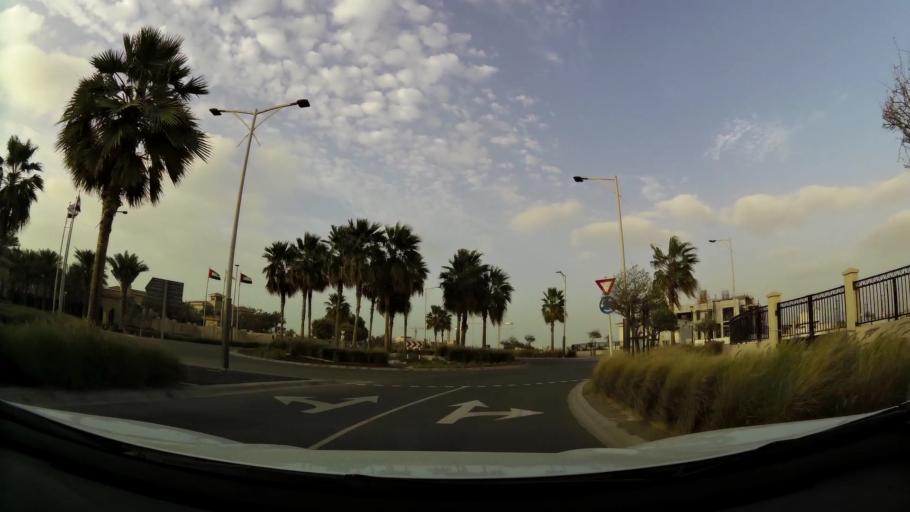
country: AE
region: Abu Dhabi
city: Abu Dhabi
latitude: 24.5368
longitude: 54.4282
